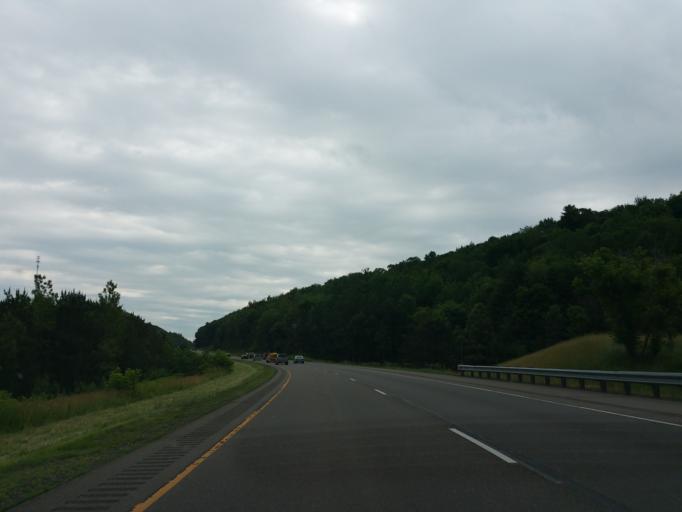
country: US
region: Wisconsin
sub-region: Trempealeau County
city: Osseo
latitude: 44.4435
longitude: -91.0794
